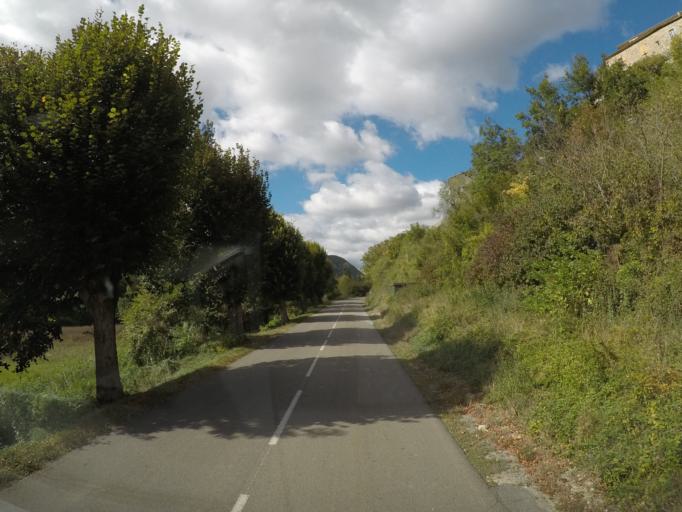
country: FR
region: Provence-Alpes-Cote d'Azur
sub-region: Departement du Vaucluse
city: Sault
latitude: 44.1673
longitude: 5.4206
